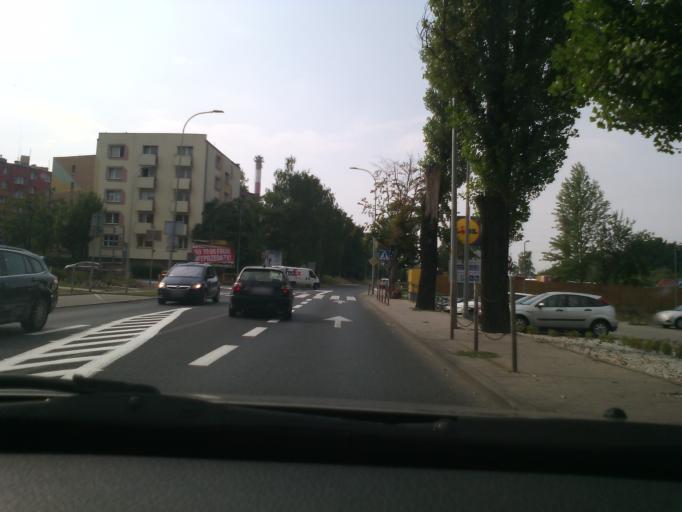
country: PL
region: Lower Silesian Voivodeship
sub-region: Powiat walbrzyski
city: Szczawno-Zdroj
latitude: 50.8113
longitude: 16.2910
